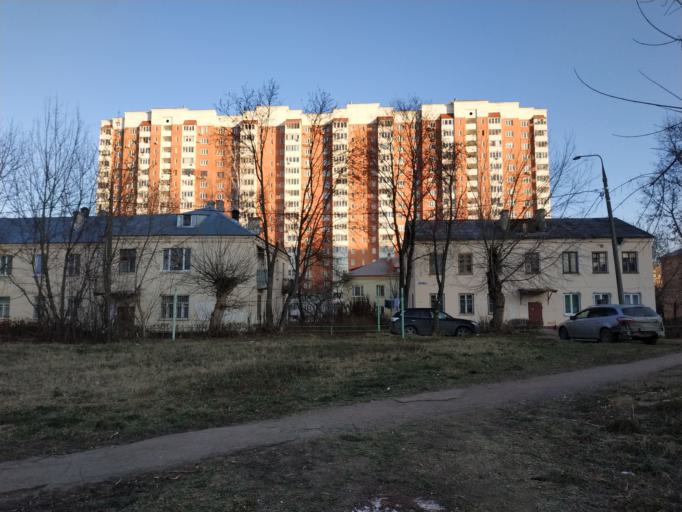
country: RU
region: Moskovskaya
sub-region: Podol'skiy Rayon
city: Podol'sk
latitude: 55.4010
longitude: 37.5568
